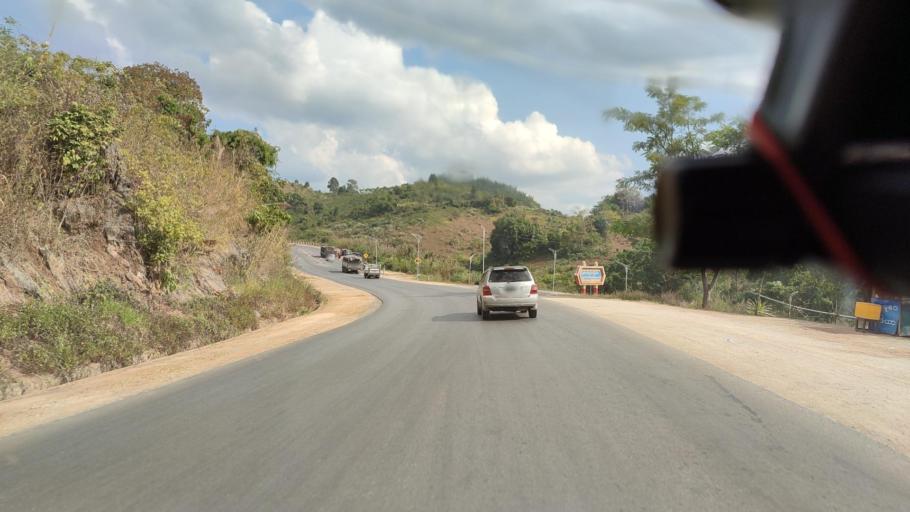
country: MM
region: Shan
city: Lashio
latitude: 23.0650
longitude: 97.7725
